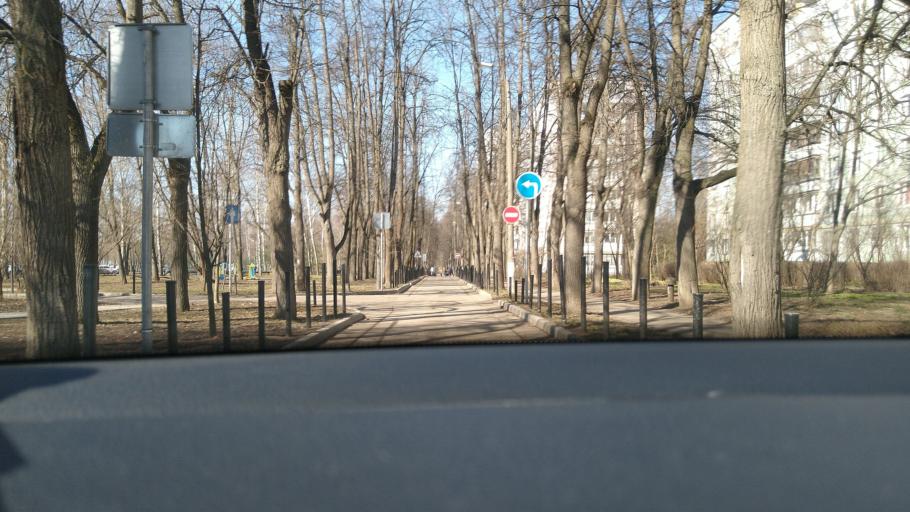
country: RU
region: Moscow
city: Rublevo
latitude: 55.7827
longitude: 37.3571
